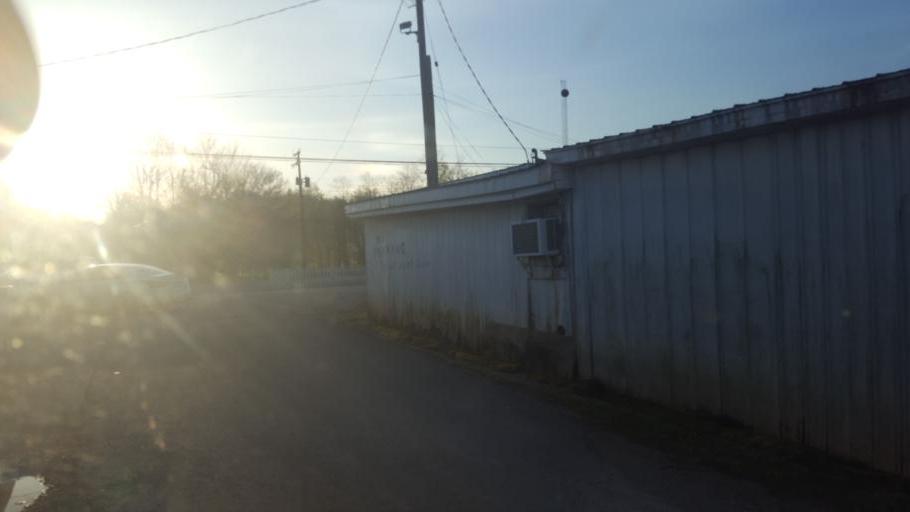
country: US
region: Kentucky
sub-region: Hart County
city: Munfordville
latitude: 37.3855
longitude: -85.9043
